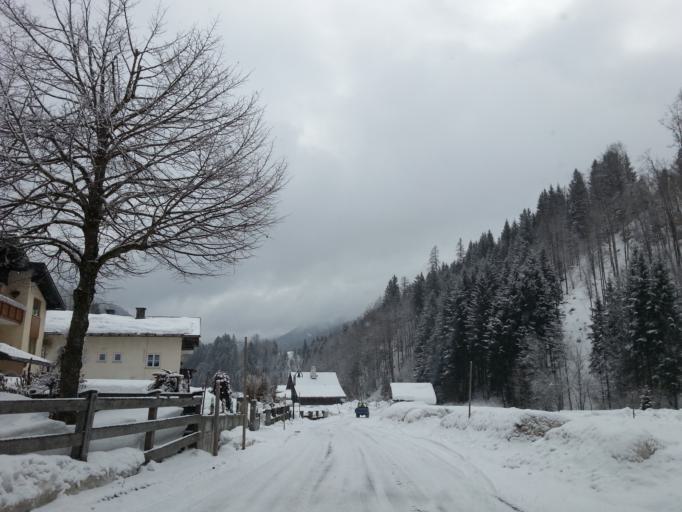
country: AT
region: Salzburg
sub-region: Politischer Bezirk Hallein
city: Abtenau
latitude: 47.4951
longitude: 13.3931
